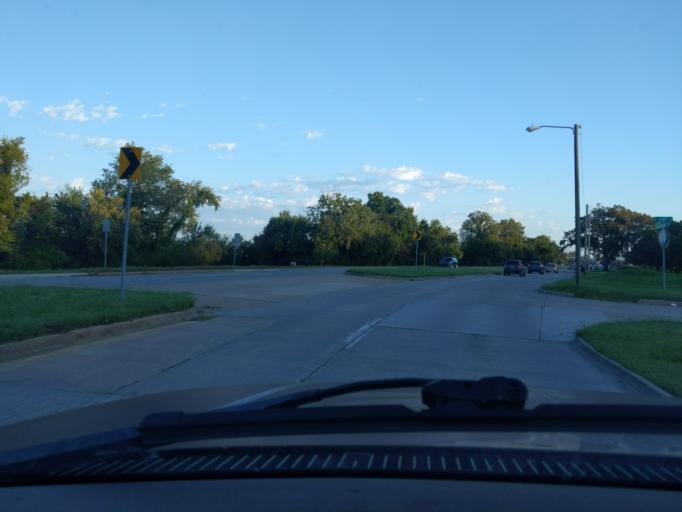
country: US
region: Oklahoma
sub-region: Tulsa County
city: Jenks
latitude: 36.0847
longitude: -95.9845
